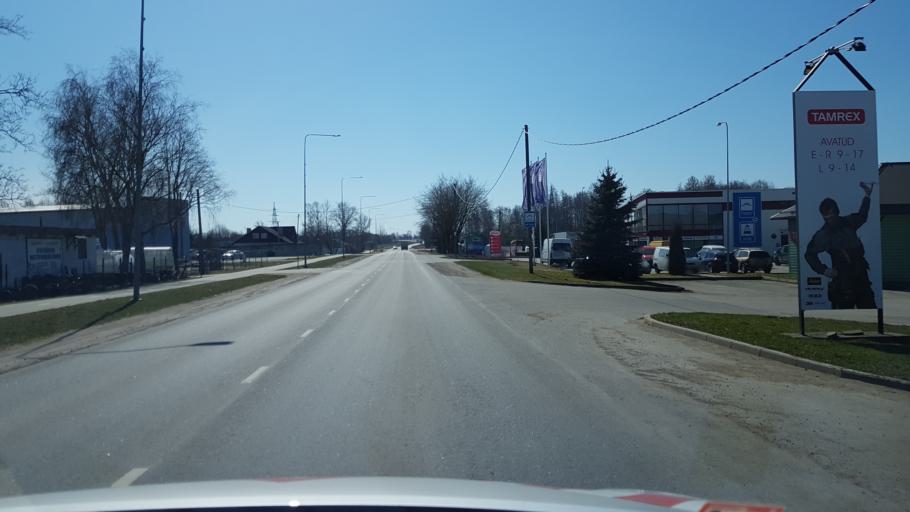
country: EE
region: Ida-Virumaa
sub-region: Johvi vald
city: Johvi
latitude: 59.3505
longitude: 27.4084
